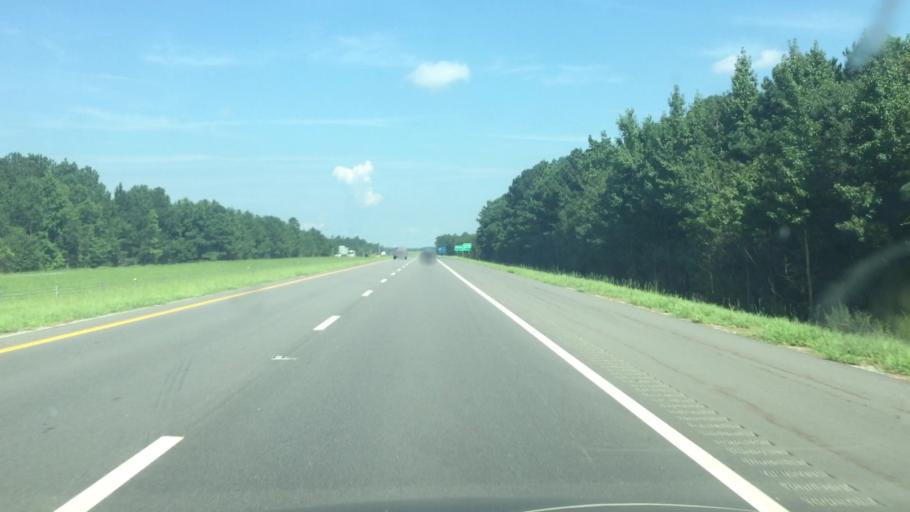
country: US
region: North Carolina
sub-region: Robeson County
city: Pembroke
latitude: 34.6635
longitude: -79.2574
